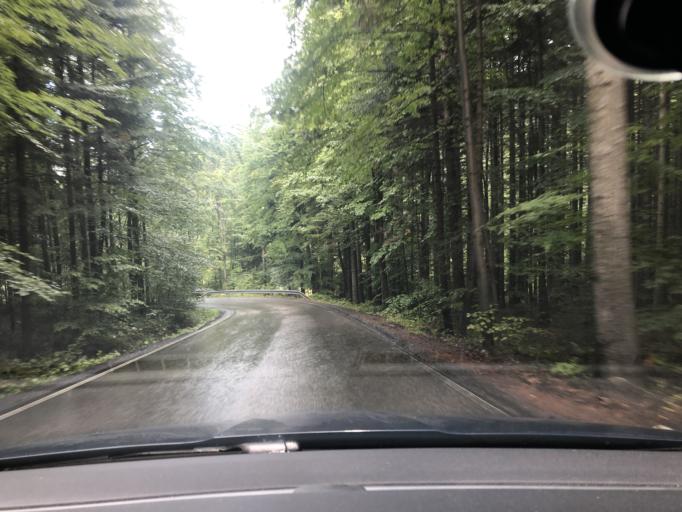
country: PL
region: Lesser Poland Voivodeship
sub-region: Powiat suski
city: Stryszawa
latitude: 49.6906
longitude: 19.5534
